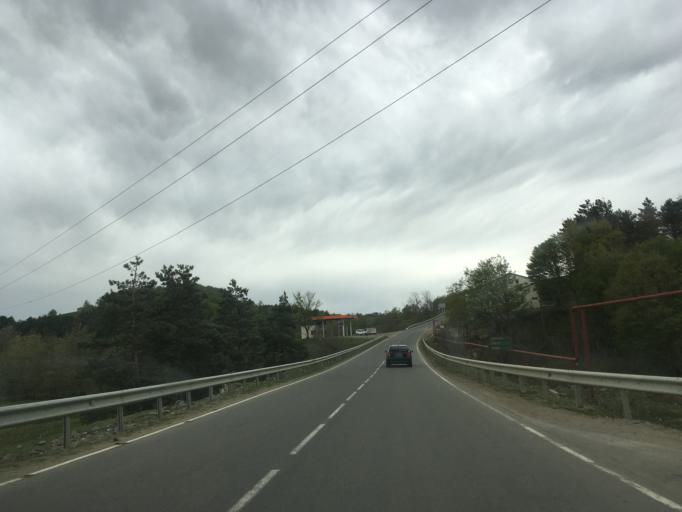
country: GE
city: Surami
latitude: 42.2381
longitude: 43.4739
